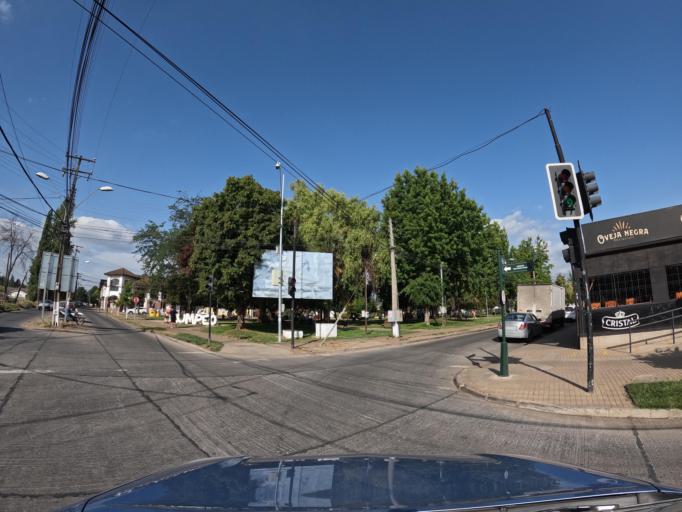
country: CL
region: Maule
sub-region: Provincia de Curico
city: Molina
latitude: -35.2817
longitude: -71.2593
